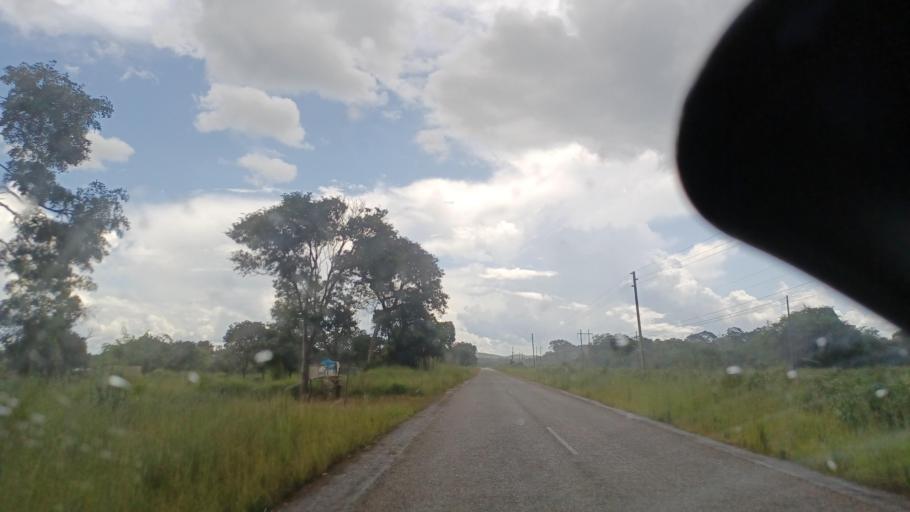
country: ZM
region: North-Western
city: Kasempa
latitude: -13.1027
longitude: 25.8879
